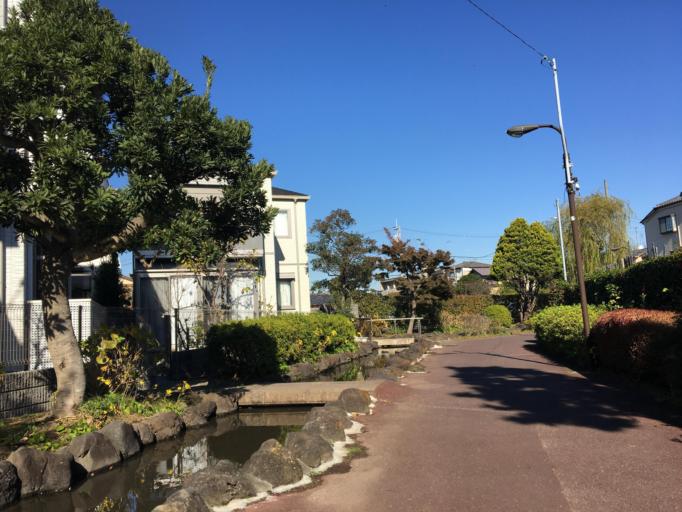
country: JP
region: Tokyo
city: Urayasu
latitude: 35.6852
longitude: 139.8948
